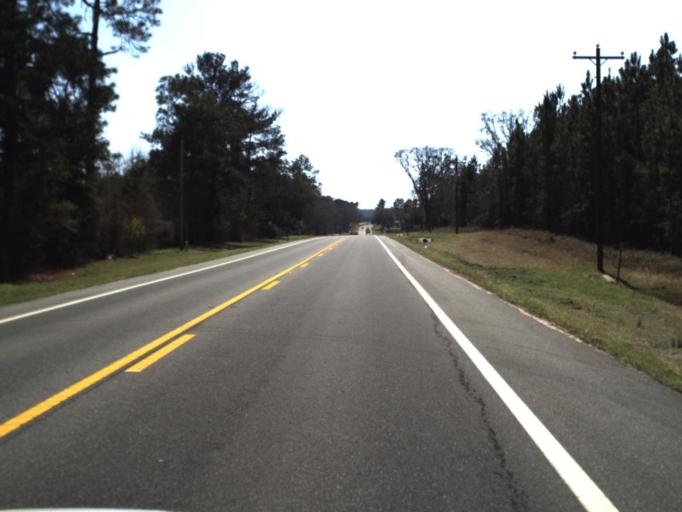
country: US
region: Florida
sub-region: Jackson County
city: Sneads
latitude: 30.7025
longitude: -85.0203
